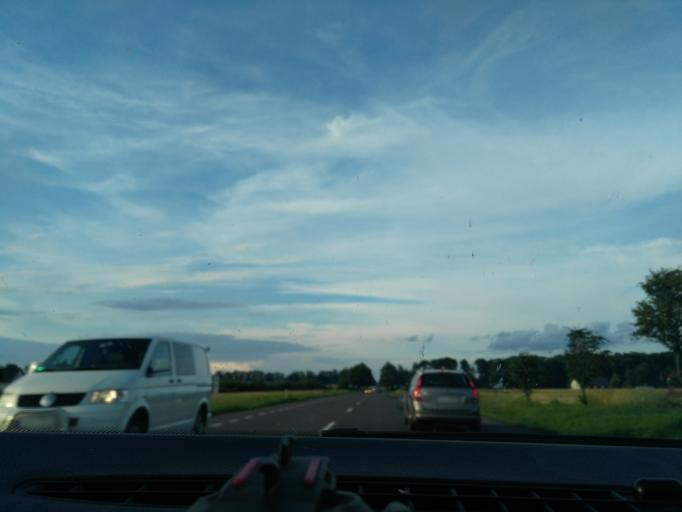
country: PL
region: Lublin Voivodeship
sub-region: Powiat krasnicki
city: Wilkolaz
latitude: 51.0235
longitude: 22.3606
